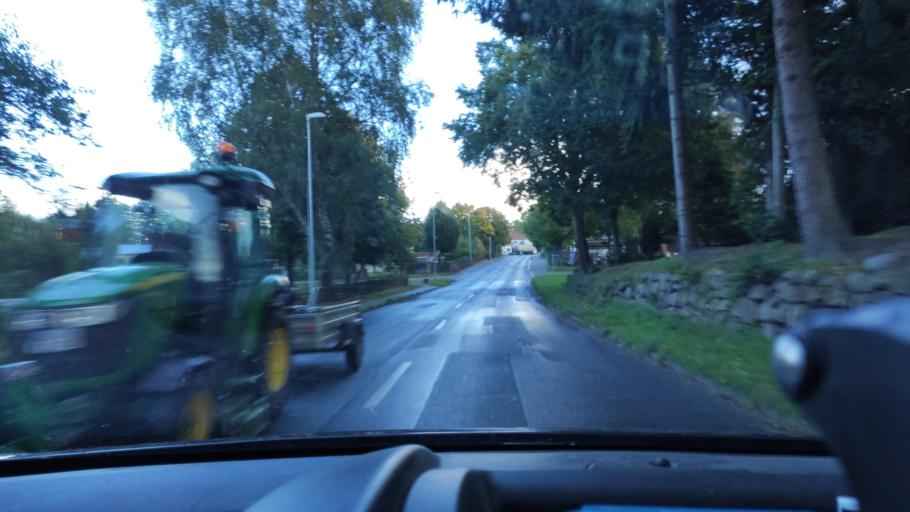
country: DE
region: Mecklenburg-Vorpommern
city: Tarnow
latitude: 53.7785
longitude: 12.0179
